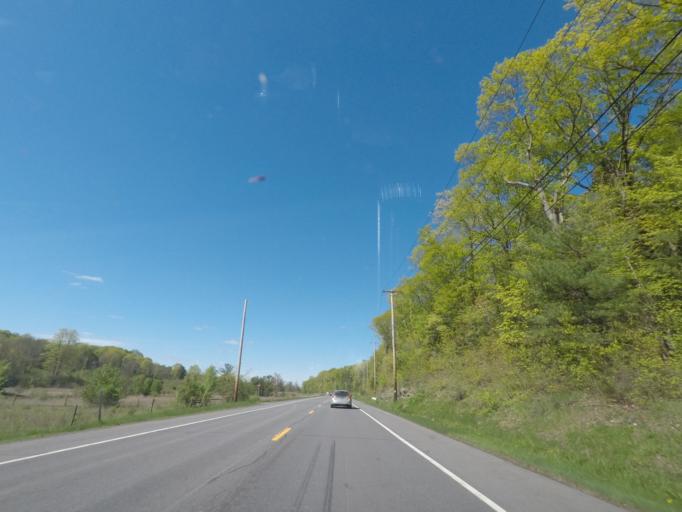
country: US
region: New York
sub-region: Albany County
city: Ravena
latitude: 42.4302
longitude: -73.8156
